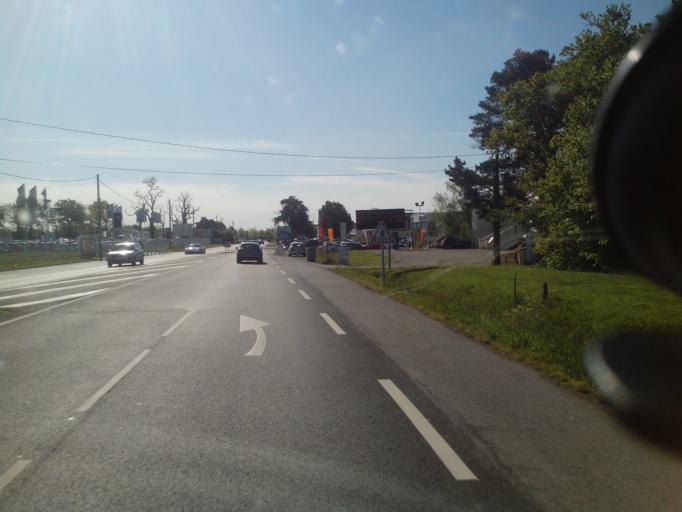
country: FR
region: Pays de la Loire
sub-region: Departement de la Loire-Atlantique
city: Orvault
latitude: 47.2540
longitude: -1.6277
